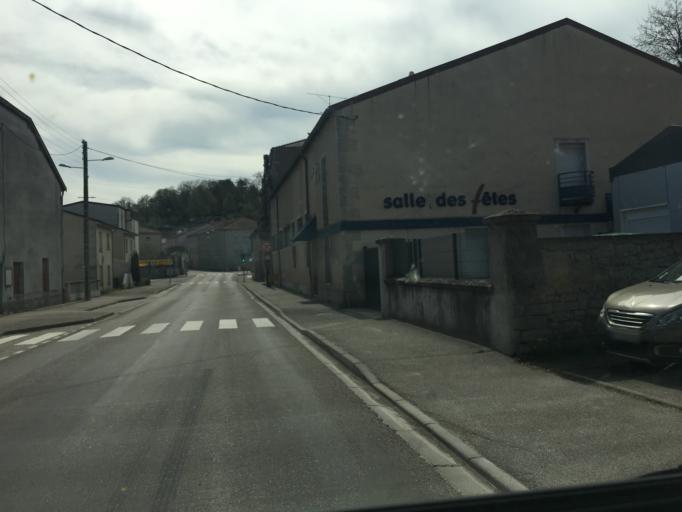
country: FR
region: Lorraine
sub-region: Departement de la Meuse
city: Lerouville
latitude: 48.7927
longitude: 5.5420
